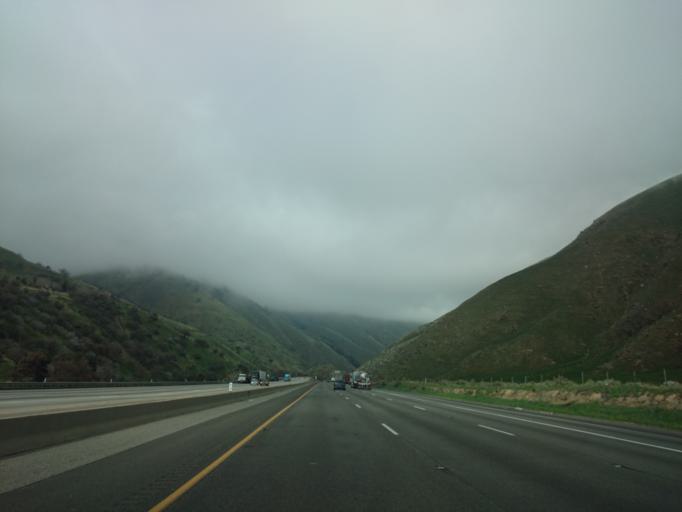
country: US
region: California
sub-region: Kern County
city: Lebec
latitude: 34.8873
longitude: -118.9055
